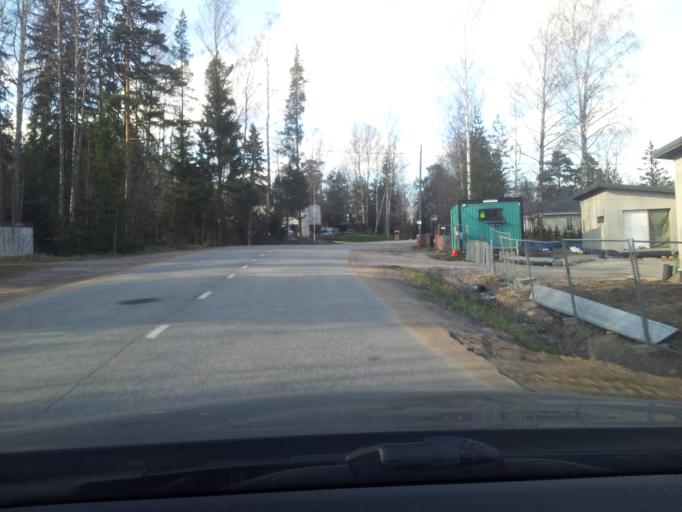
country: FI
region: Uusimaa
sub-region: Helsinki
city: Espoo
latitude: 60.1382
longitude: 24.6826
